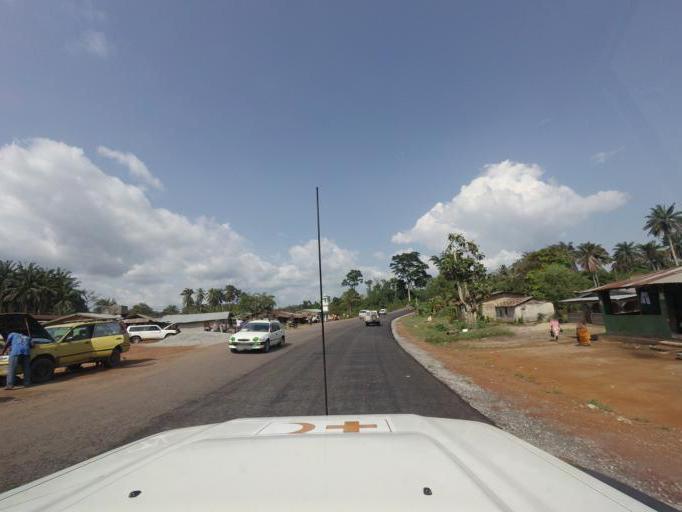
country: LR
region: Bong
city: Gbarnga
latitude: 6.8140
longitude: -9.9370
